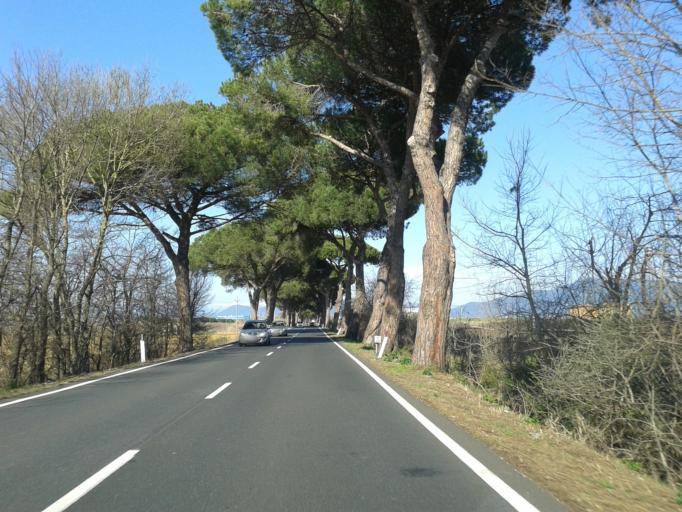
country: IT
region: Tuscany
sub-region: Province of Pisa
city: Pisa
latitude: 43.6719
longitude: 10.3750
